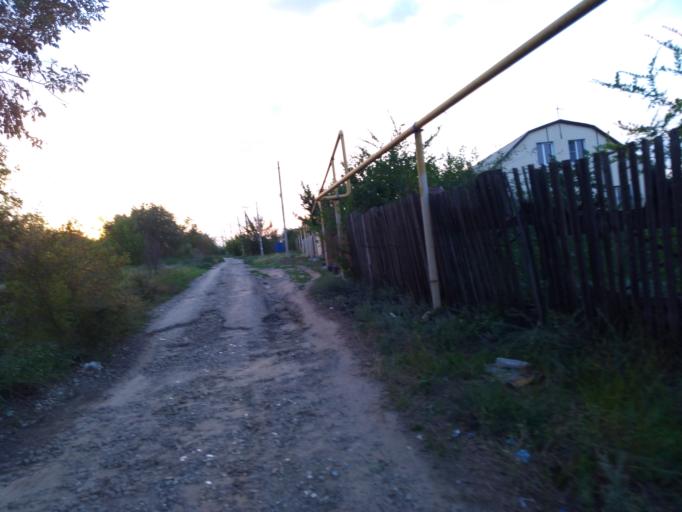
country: RU
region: Volgograd
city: Volgograd
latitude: 48.6683
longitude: 44.4552
